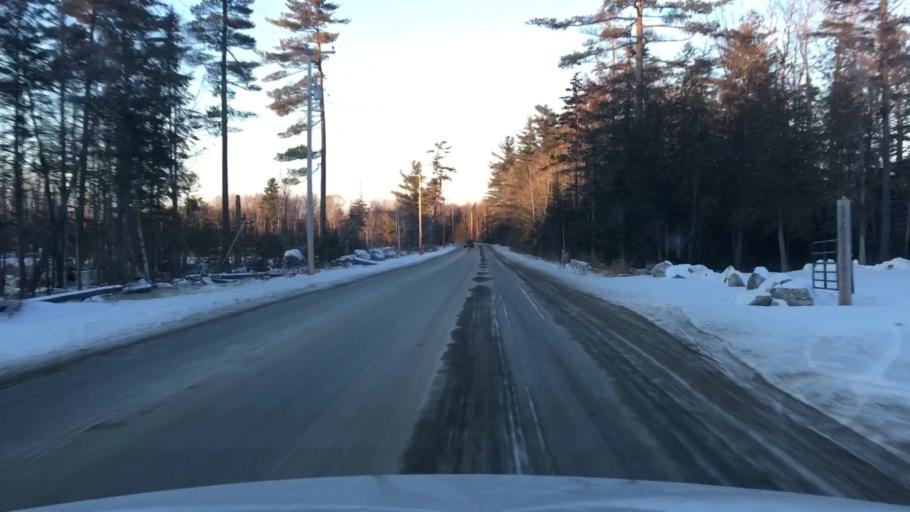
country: US
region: Maine
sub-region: Penobscot County
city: Orrington
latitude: 44.7102
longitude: -68.7537
